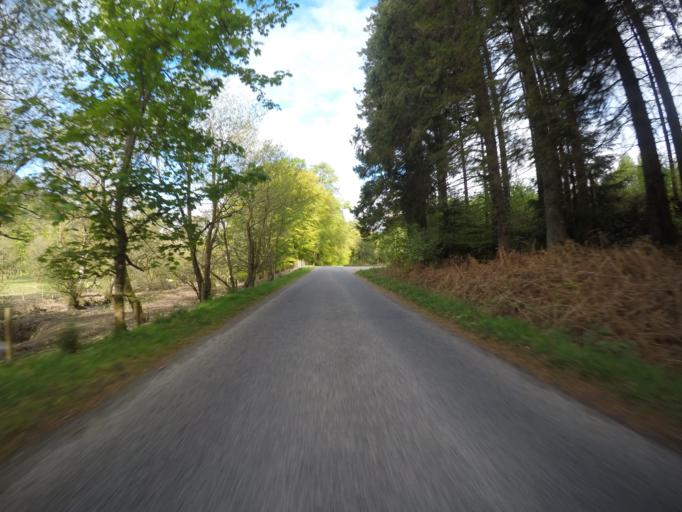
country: GB
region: Scotland
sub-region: Highland
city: Fort William
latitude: 56.6820
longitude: -5.0911
